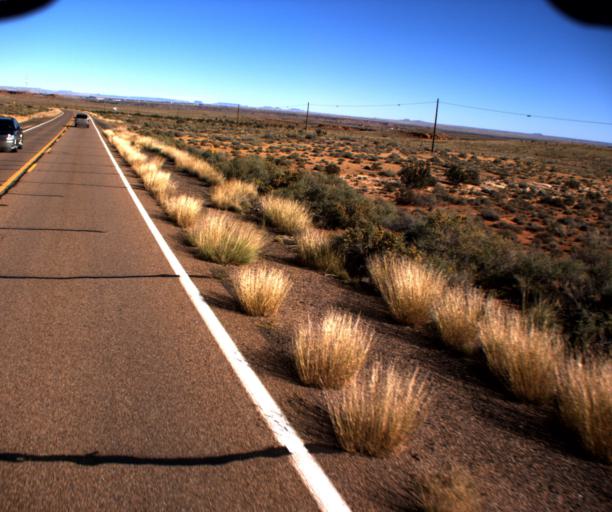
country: US
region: Arizona
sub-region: Navajo County
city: Holbrook
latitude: 34.8464
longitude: -110.1474
